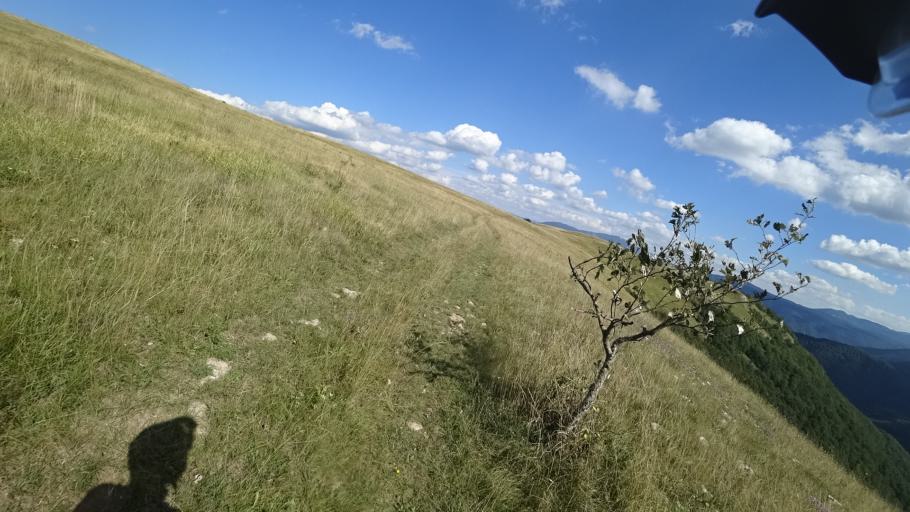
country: HR
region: Zadarska
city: Gracac
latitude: 44.3709
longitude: 16.0661
